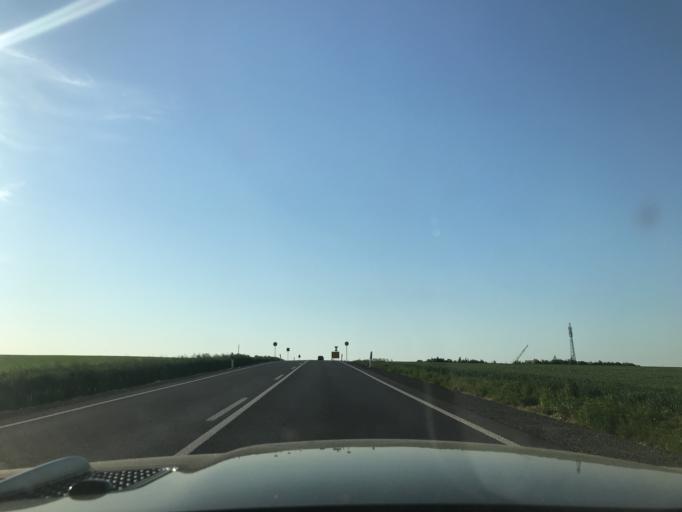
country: DE
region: Thuringia
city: Hochheim
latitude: 51.0504
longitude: 10.6556
